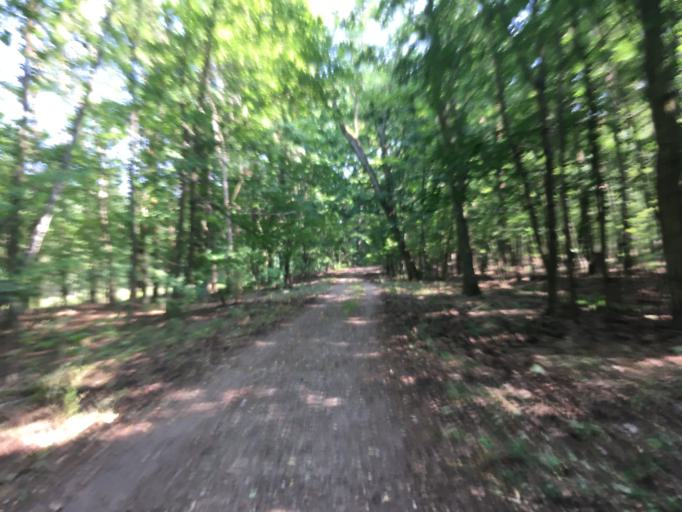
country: DE
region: Berlin
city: Schmockwitz
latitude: 52.3770
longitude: 13.6774
